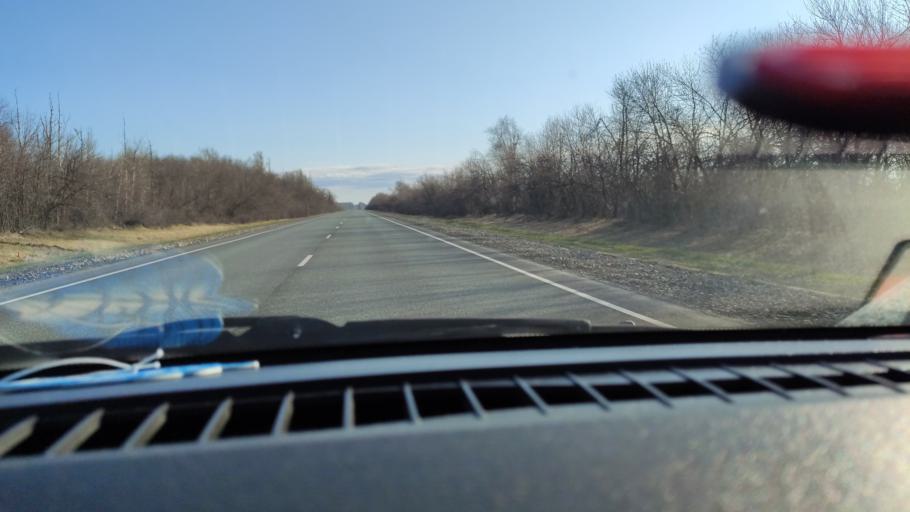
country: RU
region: Saratov
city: Khvalynsk
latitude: 52.5968
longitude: 48.1390
